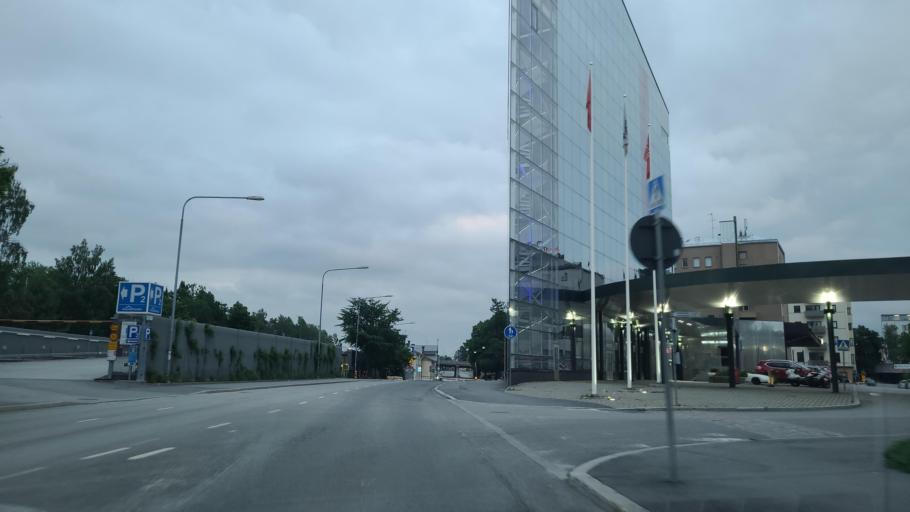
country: FI
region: Ostrobothnia
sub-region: Vaasa
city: Vaasa
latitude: 63.0985
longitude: 21.6186
